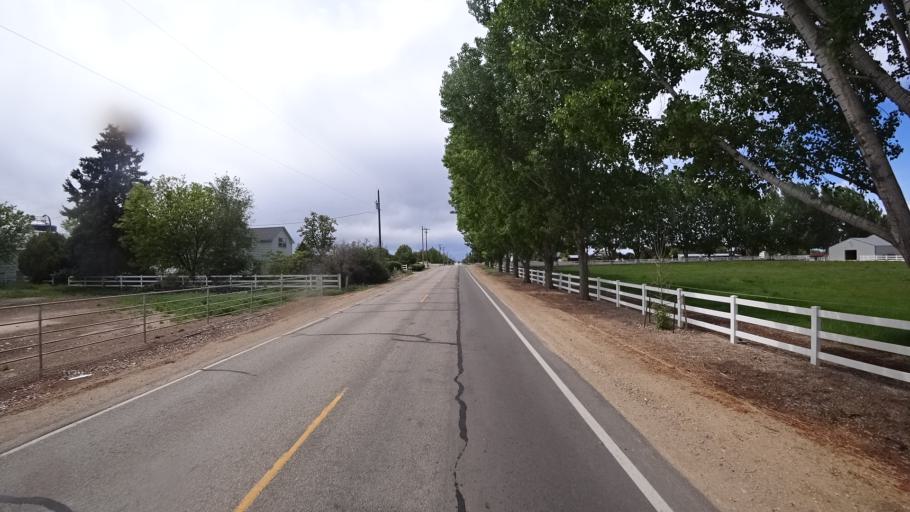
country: US
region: Idaho
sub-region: Ada County
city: Meridian
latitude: 43.5755
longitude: -116.4220
